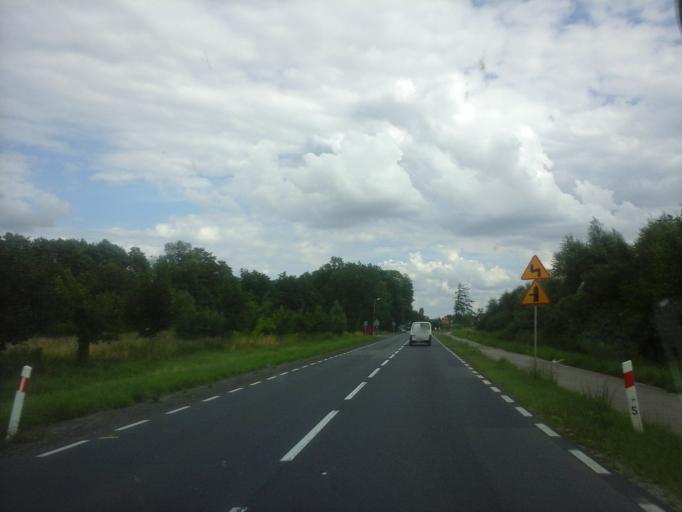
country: PL
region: West Pomeranian Voivodeship
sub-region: Powiat stargardzki
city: Stargard Szczecinski
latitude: 53.3232
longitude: 15.0787
